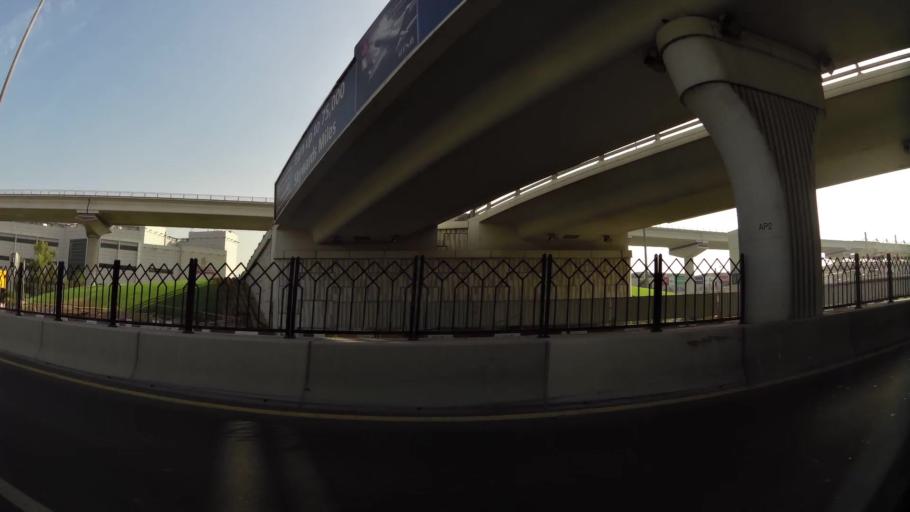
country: AE
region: Ash Shariqah
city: Sharjah
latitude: 25.2491
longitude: 55.3495
